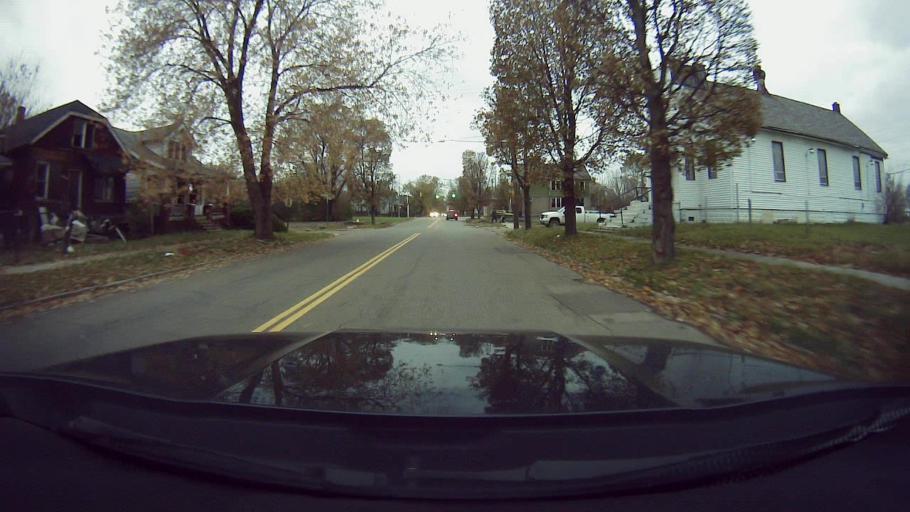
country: US
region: Michigan
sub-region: Wayne County
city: Hamtramck
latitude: 42.3799
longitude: -82.9996
